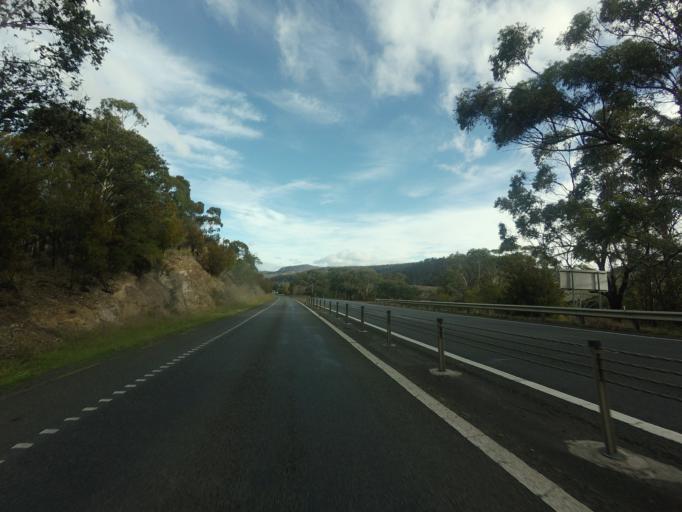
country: AU
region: Tasmania
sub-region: Brighton
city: Bridgewater
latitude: -42.5878
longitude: 147.2247
